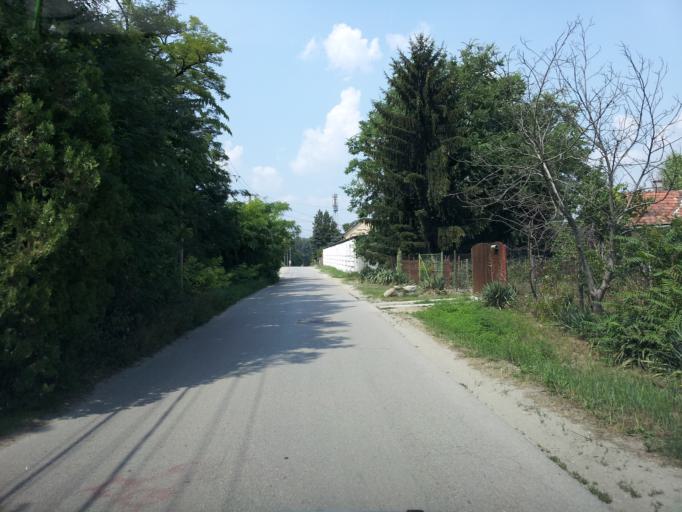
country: HU
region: Pest
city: Szigethalom
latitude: 47.3139
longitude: 19.0227
